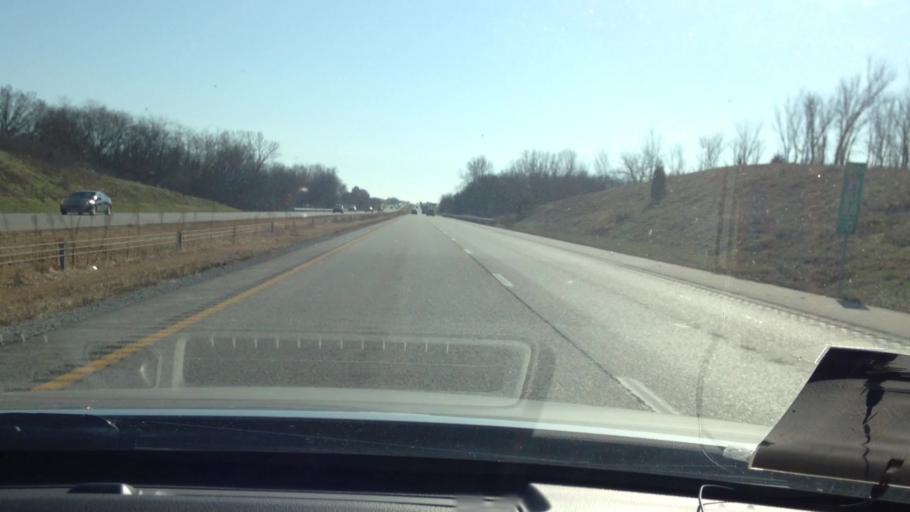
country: US
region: Missouri
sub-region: Platte County
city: Platte City
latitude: 39.4879
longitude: -94.7866
